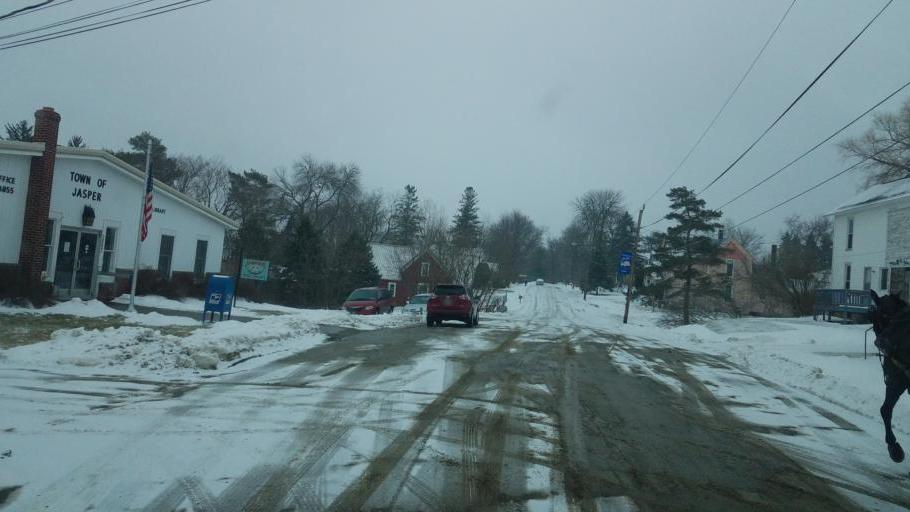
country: US
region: New York
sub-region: Steuben County
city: Canisteo
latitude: 42.1217
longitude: -77.5037
